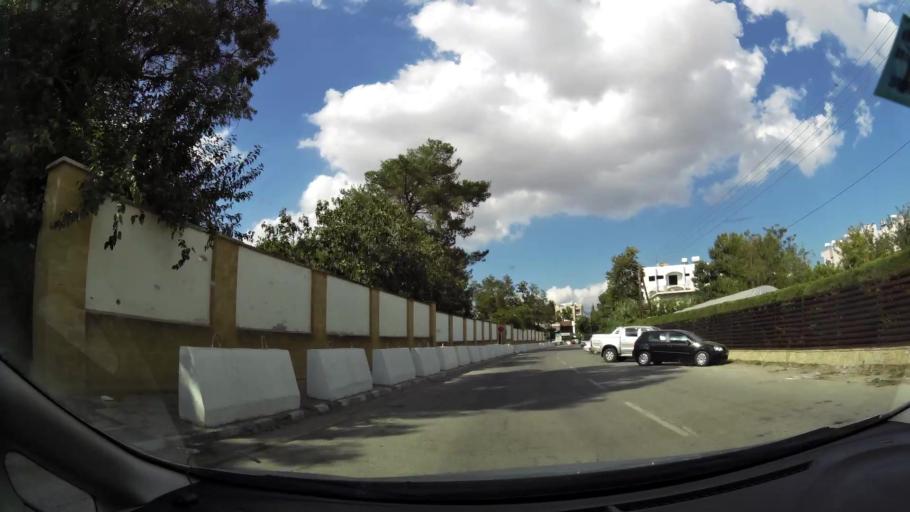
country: CY
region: Lefkosia
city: Nicosia
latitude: 35.1806
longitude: 33.3512
